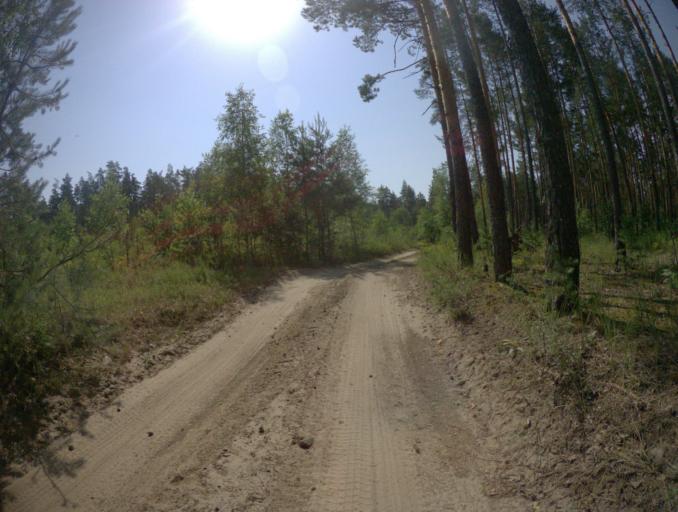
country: RU
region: Vladimir
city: Vyazniki
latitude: 56.3709
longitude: 42.1904
